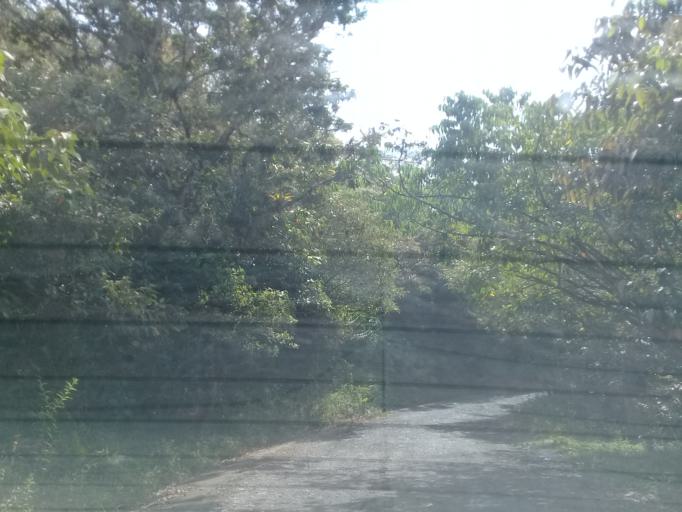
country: CO
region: Cundinamarca
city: Gachala
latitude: 4.7029
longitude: -73.4892
